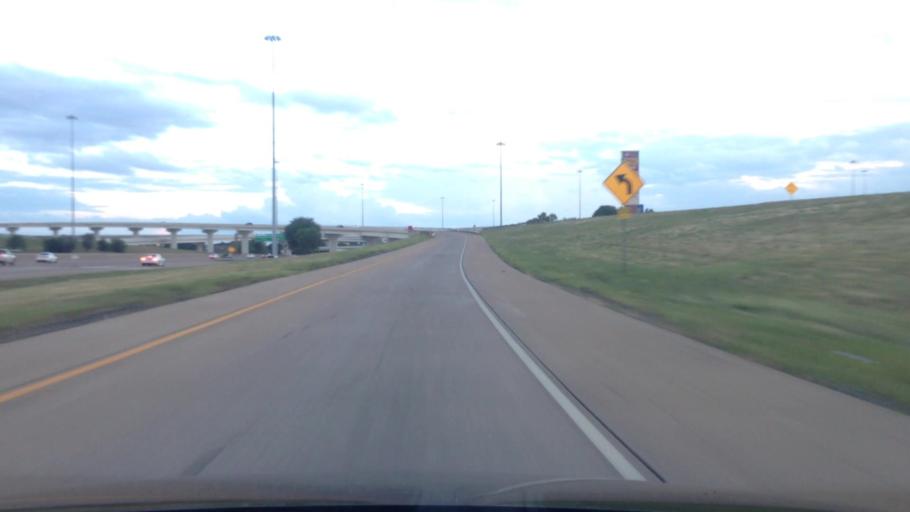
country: US
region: Texas
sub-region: Tarrant County
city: Richland Hills
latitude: 32.7654
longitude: -97.2133
